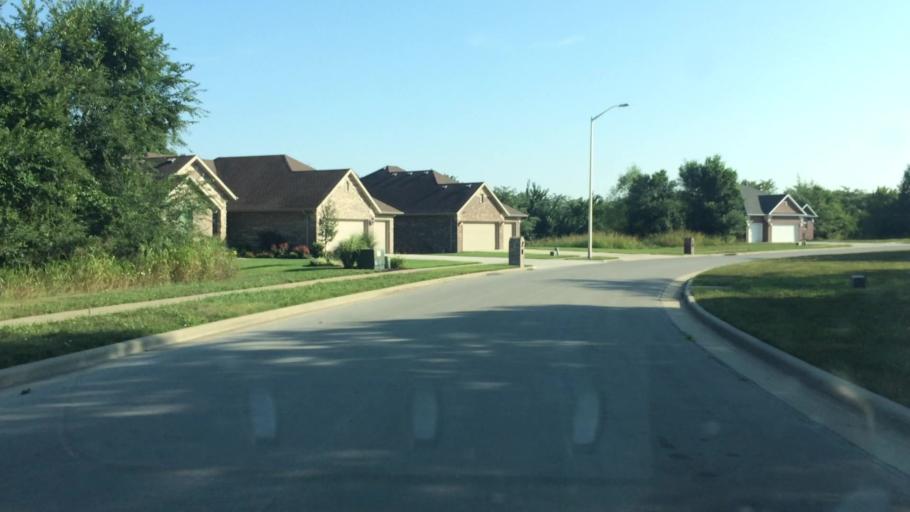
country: US
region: Missouri
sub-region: Greene County
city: Springfield
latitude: 37.2680
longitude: -93.2767
